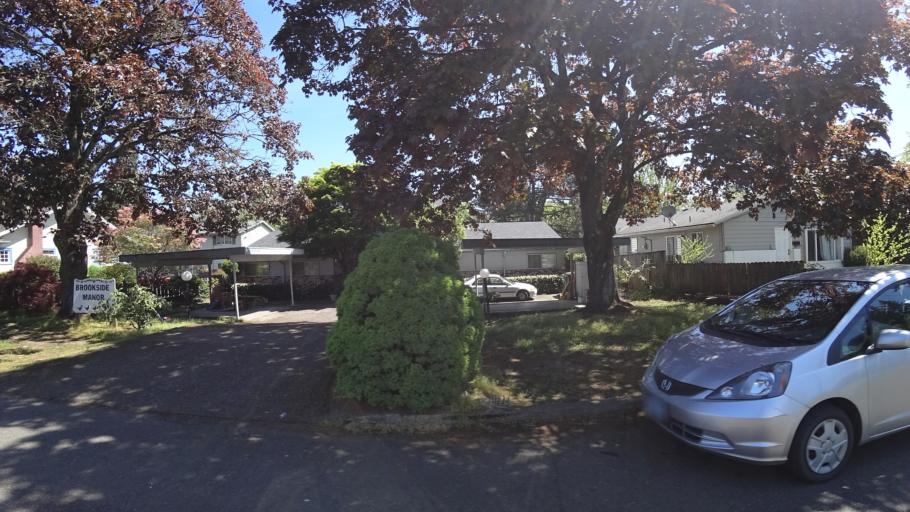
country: US
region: Oregon
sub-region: Clackamas County
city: Milwaukie
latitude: 45.4669
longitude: -122.6430
